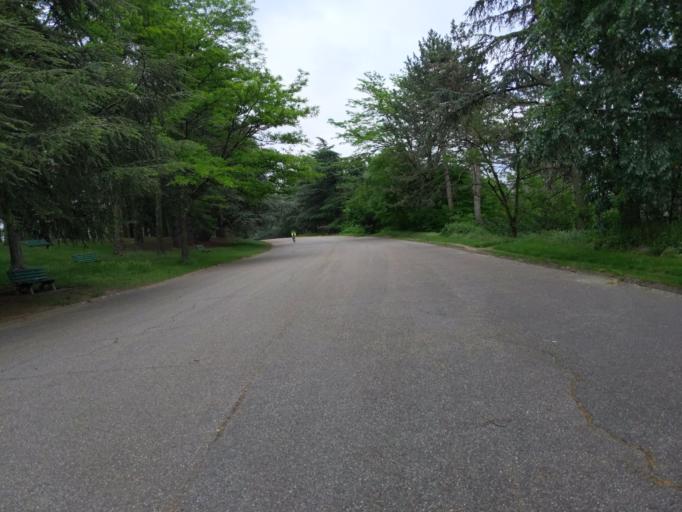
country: FR
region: Rhone-Alpes
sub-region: Departement du Rhone
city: Bron
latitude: 45.7232
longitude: 4.8994
